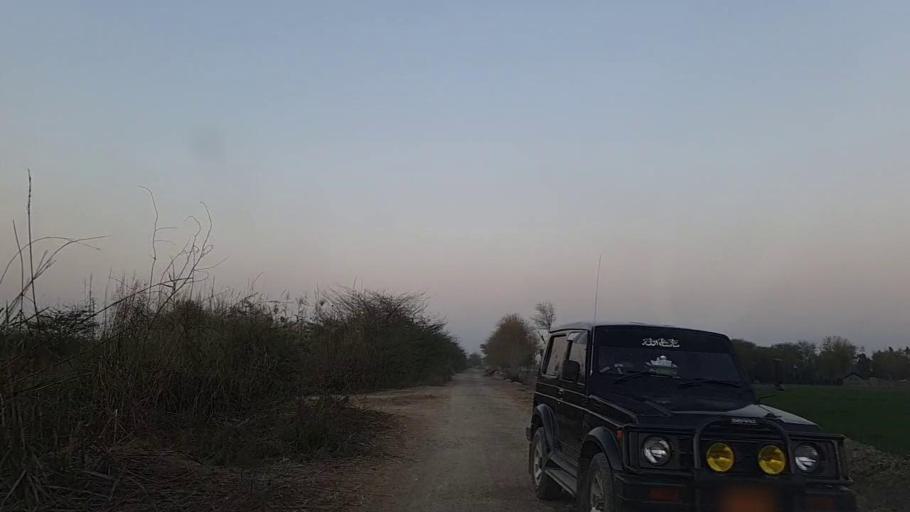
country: PK
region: Sindh
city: Bandhi
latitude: 26.6092
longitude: 68.3751
